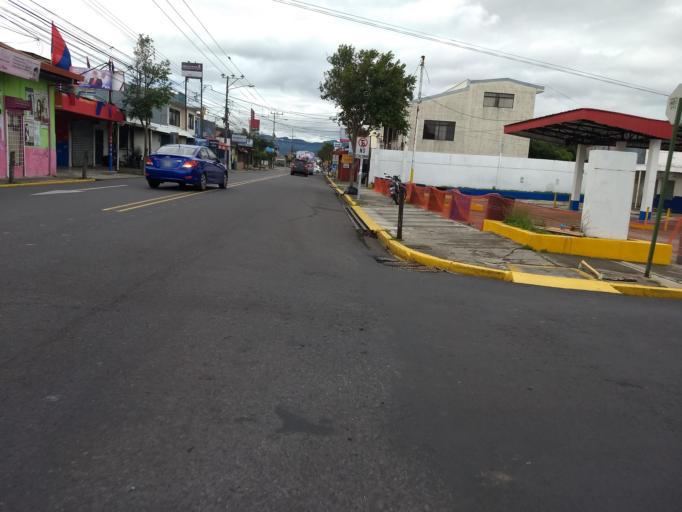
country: CR
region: San Jose
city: San Juan
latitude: 9.9598
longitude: -84.0784
